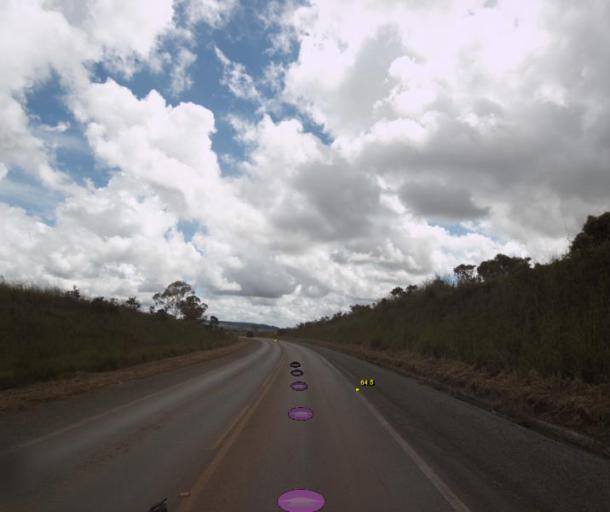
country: BR
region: Goias
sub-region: Pirenopolis
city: Pirenopolis
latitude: -15.7552
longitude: -48.7444
